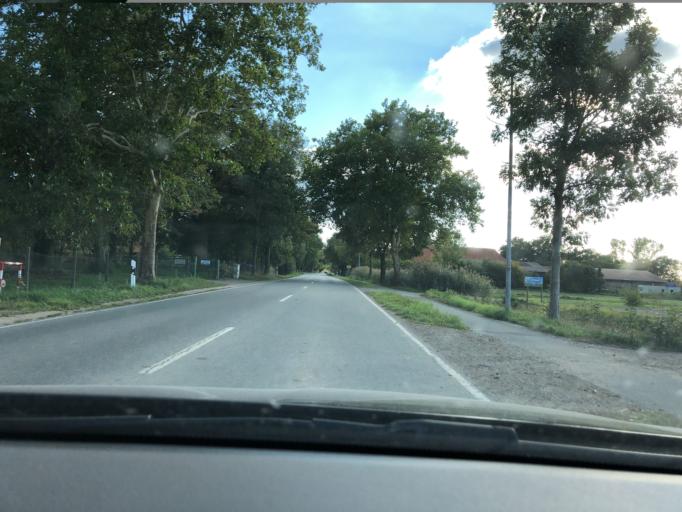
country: DE
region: Lower Saxony
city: Stuhr
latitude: 53.0336
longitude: 8.7589
